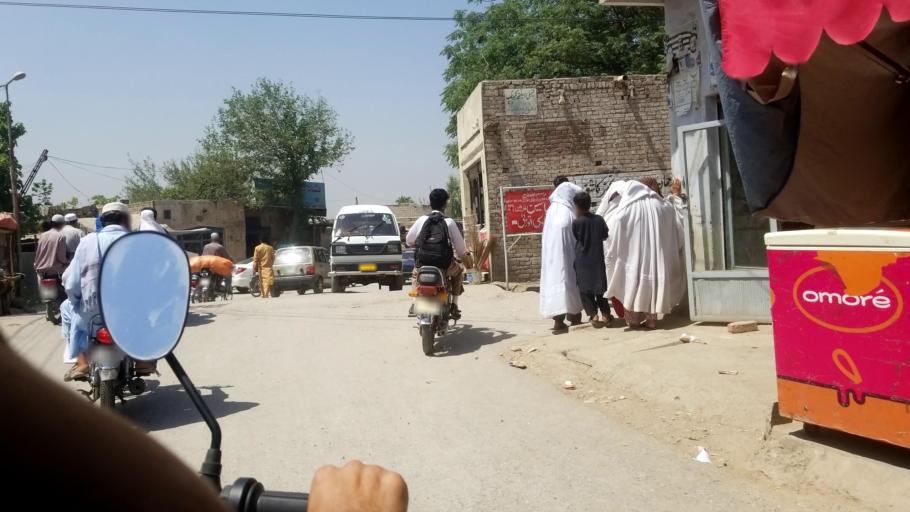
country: PK
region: Khyber Pakhtunkhwa
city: Peshawar
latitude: 34.0306
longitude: 71.4845
